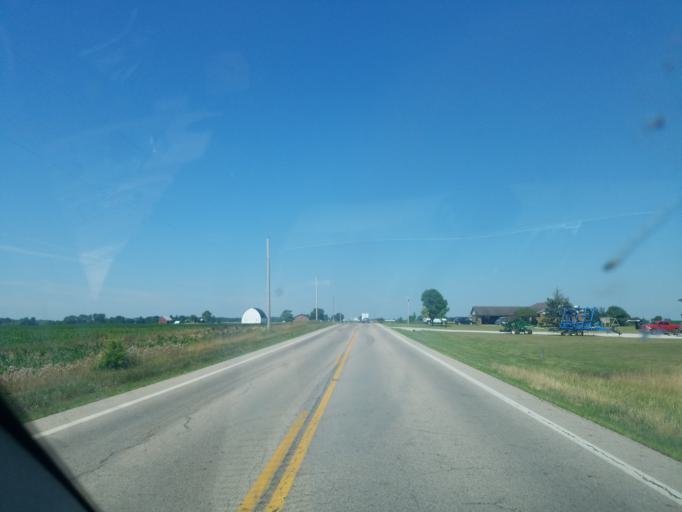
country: US
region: Ohio
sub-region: Shelby County
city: Botkins
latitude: 40.4385
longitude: -84.2145
